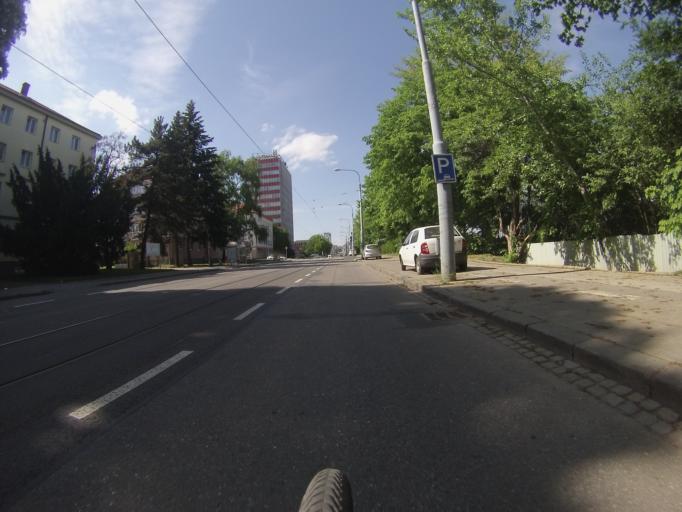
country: CZ
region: South Moravian
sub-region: Mesto Brno
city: Brno
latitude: 49.2156
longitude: 16.5895
